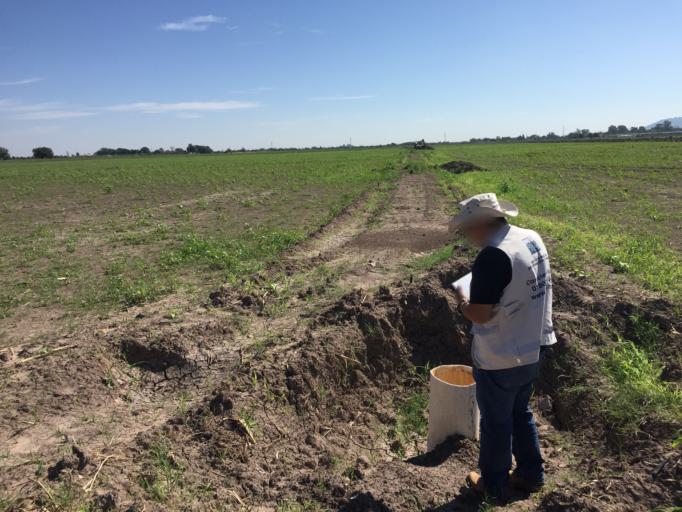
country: MX
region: Durango
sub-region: Gomez Palacio
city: San Felipe
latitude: 25.7270
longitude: -103.3718
